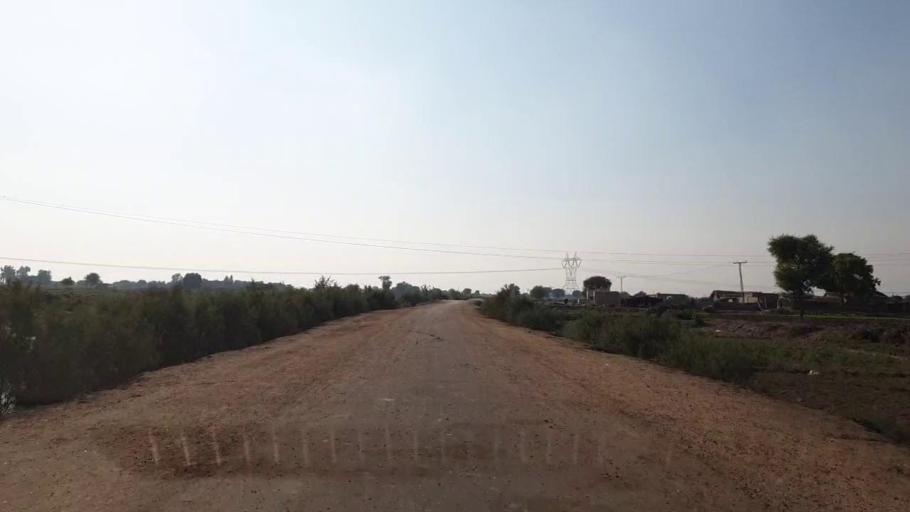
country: PK
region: Sindh
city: Sehwan
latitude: 26.4388
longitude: 67.8041
